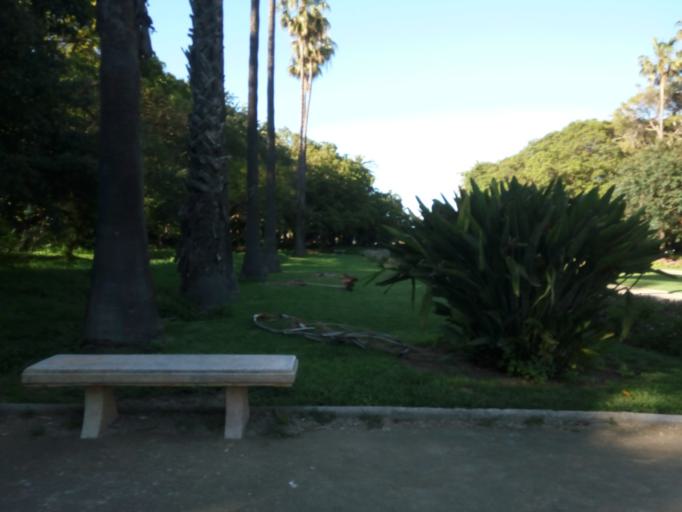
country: DZ
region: Alger
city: Algiers
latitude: 36.7503
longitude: 3.0748
